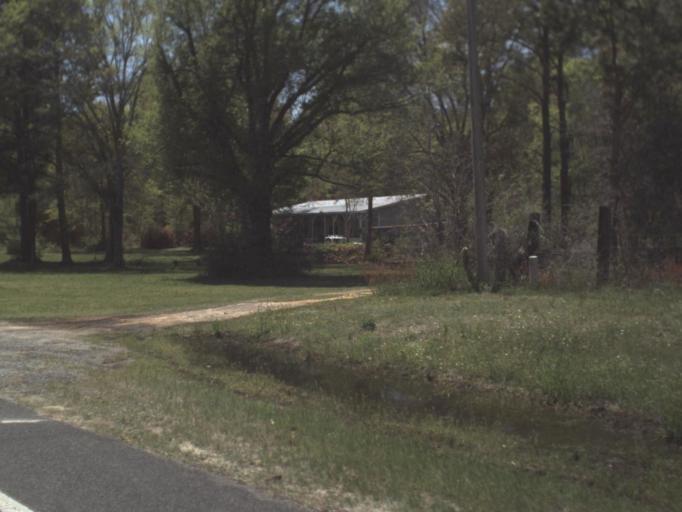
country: US
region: Florida
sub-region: Walton County
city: DeFuniak Springs
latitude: 30.8437
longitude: -85.9497
